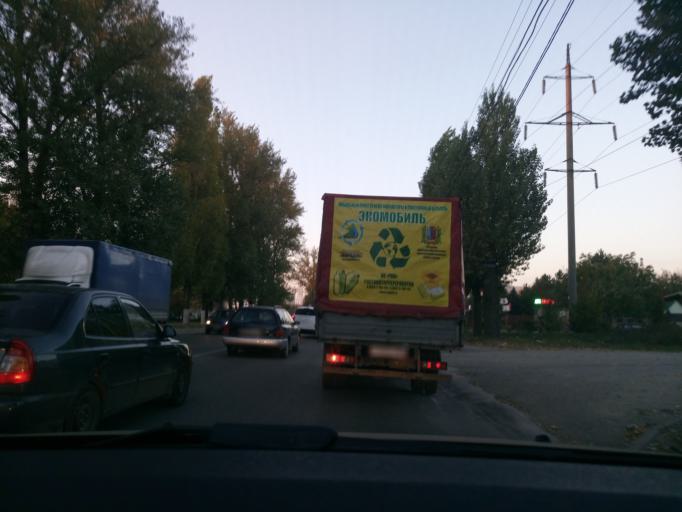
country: RU
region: Rostov
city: Kalinin
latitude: 47.2428
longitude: 39.6141
